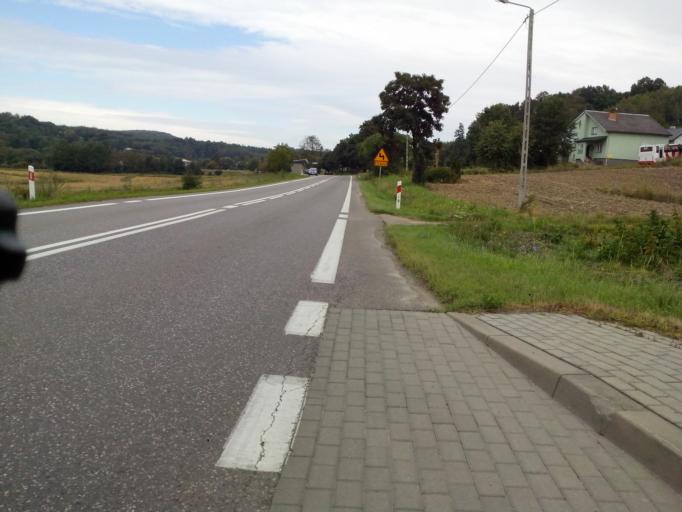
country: PL
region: Subcarpathian Voivodeship
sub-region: Powiat brzozowski
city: Domaradz
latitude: 49.7695
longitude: 21.9539
